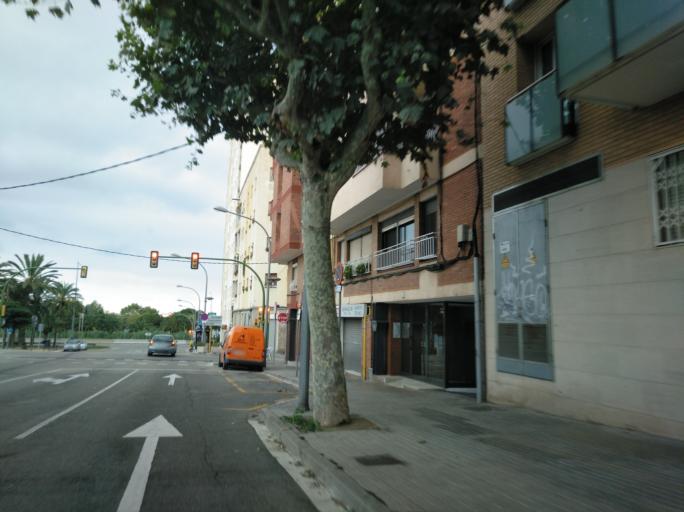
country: ES
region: Catalonia
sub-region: Provincia de Barcelona
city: Mataro
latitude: 41.5418
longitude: 2.4557
